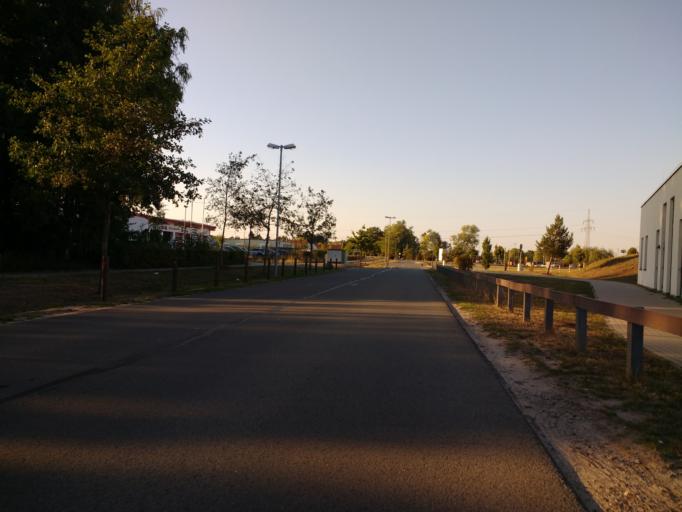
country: DE
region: Lower Saxony
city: Gifhorn
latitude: 52.4962
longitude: 10.5464
